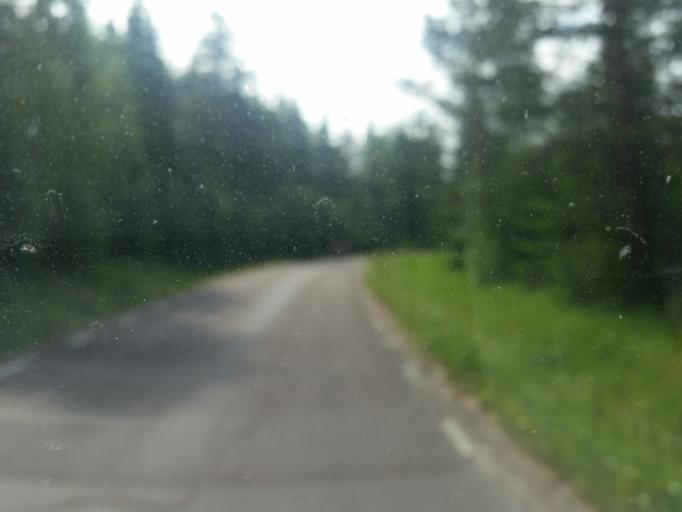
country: SE
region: Dalarna
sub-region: Gagnefs Kommun
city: Gagnef
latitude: 60.6751
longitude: 15.1721
